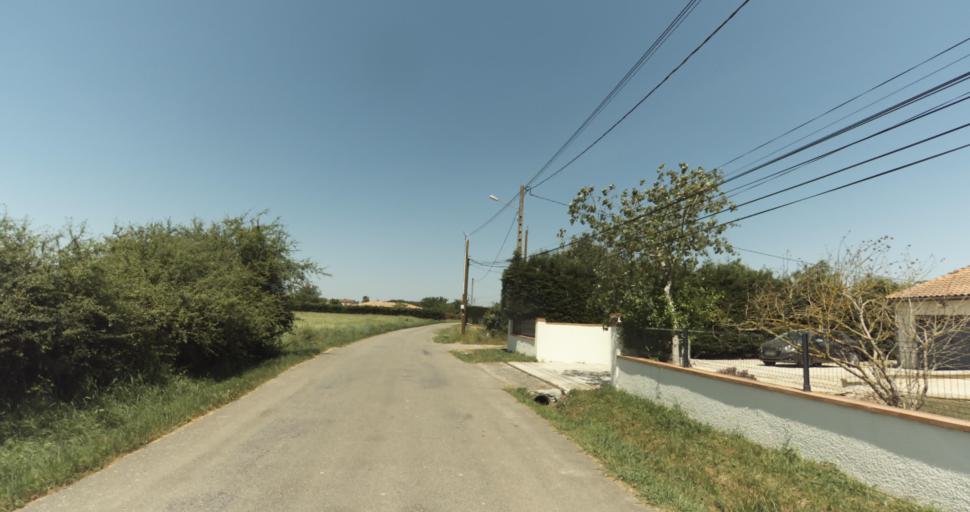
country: FR
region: Midi-Pyrenees
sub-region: Departement de la Haute-Garonne
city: Levignac
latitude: 43.6370
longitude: 1.1879
